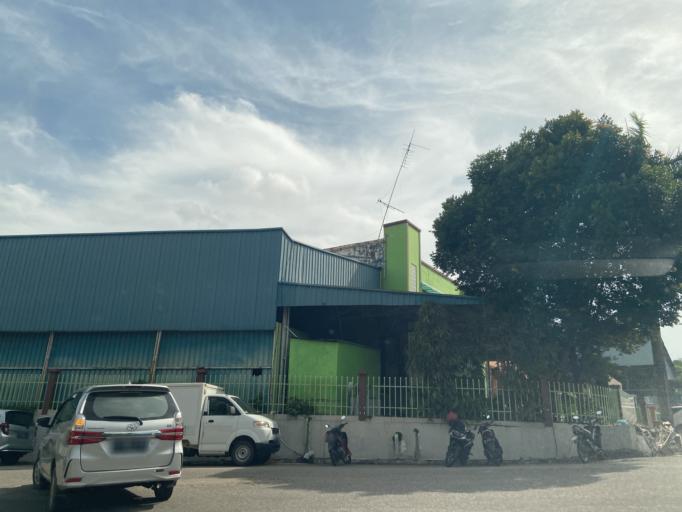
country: SG
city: Singapore
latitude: 1.1496
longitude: 104.0201
